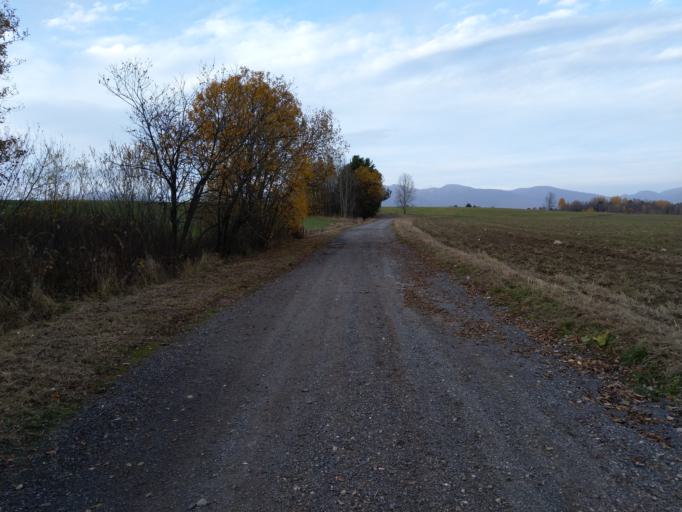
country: SK
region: Zilinsky
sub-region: Okres Liptovsky Mikulas
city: Hybe
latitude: 49.0586
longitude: 19.8261
